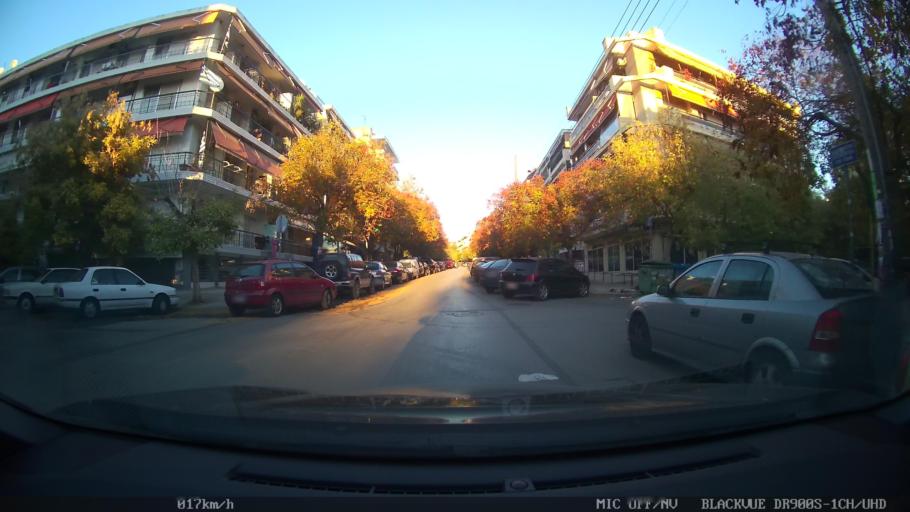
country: GR
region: Central Macedonia
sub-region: Nomos Thessalonikis
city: Triandria
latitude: 40.6068
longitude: 22.9792
